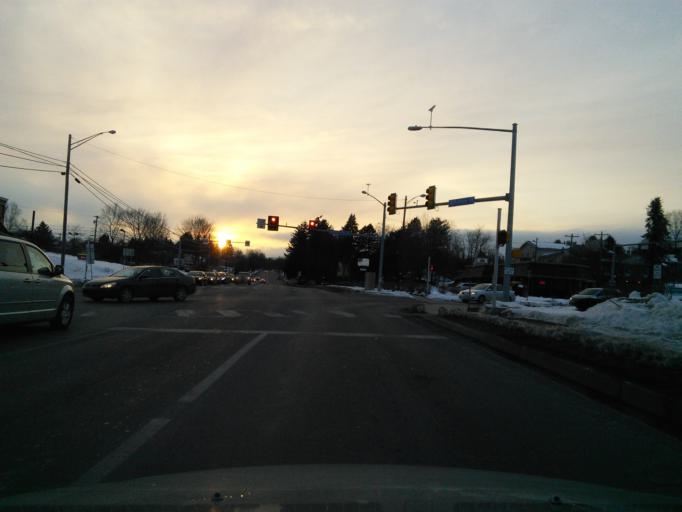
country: US
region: Pennsylvania
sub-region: Centre County
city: State College
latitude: 40.7854
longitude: -77.8367
